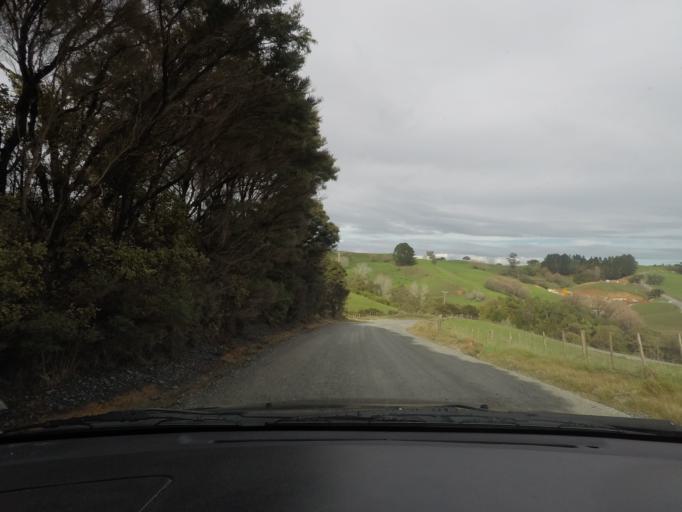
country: NZ
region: Auckland
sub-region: Auckland
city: Warkworth
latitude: -36.4470
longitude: 174.7505
